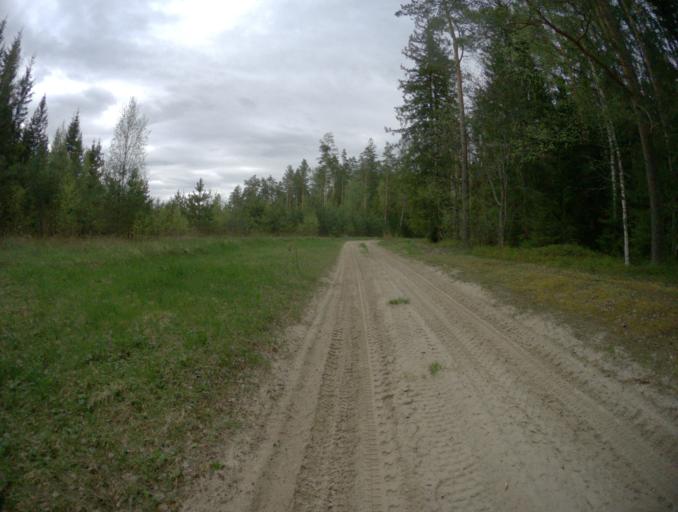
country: RU
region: Vladimir
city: Golovino
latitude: 55.8986
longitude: 40.4272
